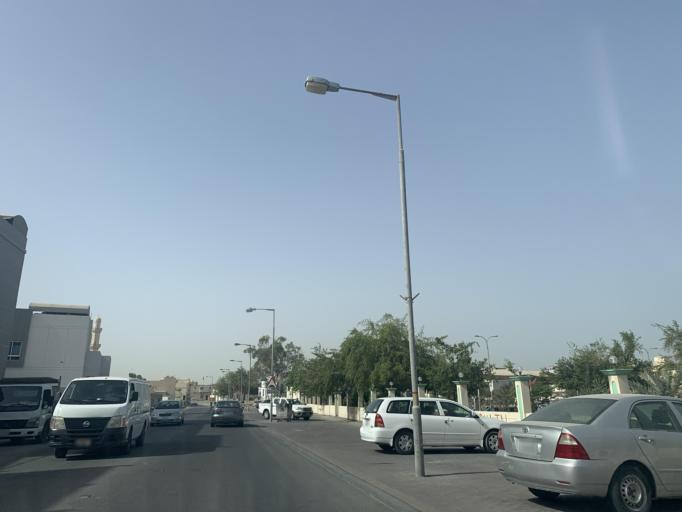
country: BH
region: Northern
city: Sitrah
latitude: 26.1644
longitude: 50.6081
